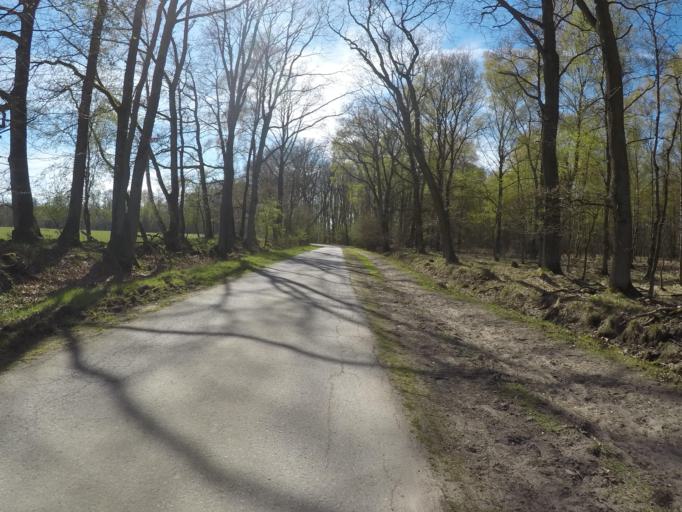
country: DE
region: Hamburg
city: Wohldorf-Ohlstedt
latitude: 53.7165
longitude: 10.1563
